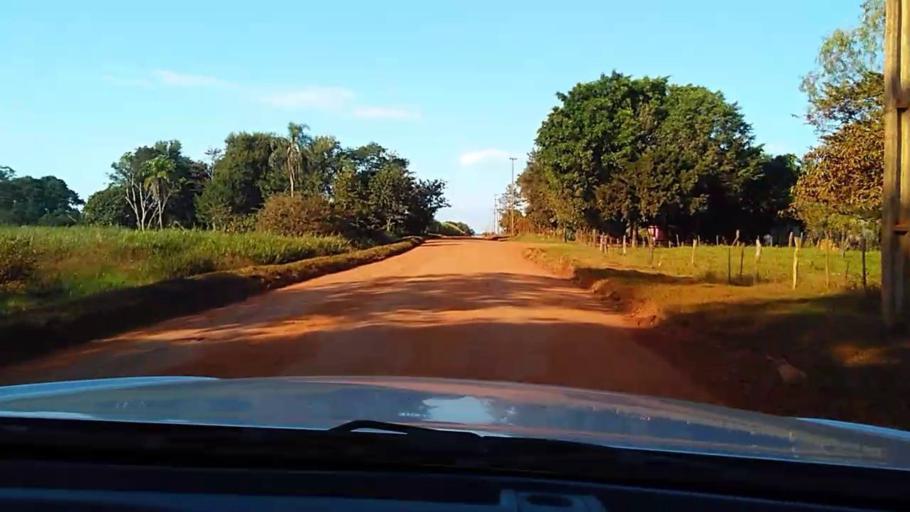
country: PY
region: Alto Parana
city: Doctor Juan Leon Mallorquin
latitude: -25.6923
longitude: -55.3781
